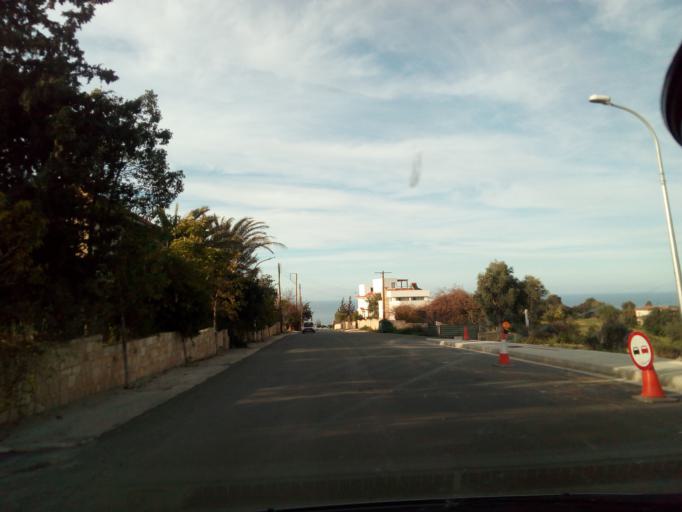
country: CY
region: Pafos
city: Polis
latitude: 35.0311
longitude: 32.3627
